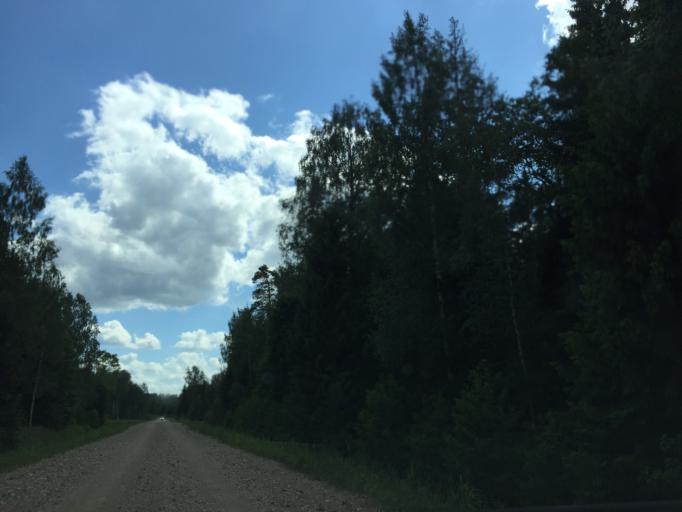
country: LV
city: Tireli
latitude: 56.8460
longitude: 23.6965
